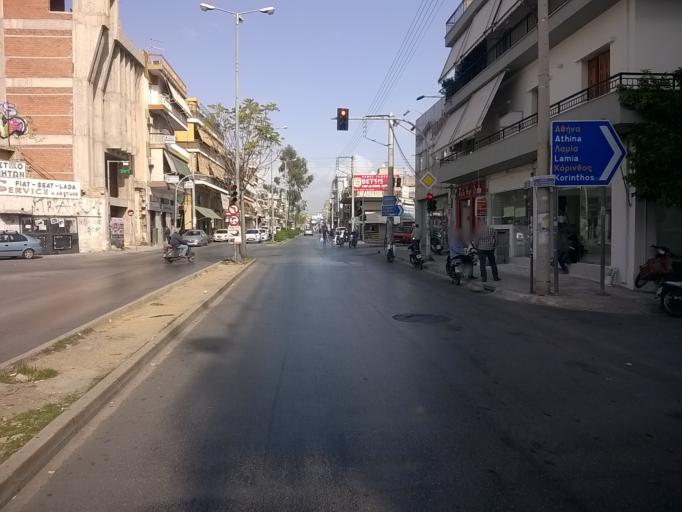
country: GR
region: Attica
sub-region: Nomos Piraios
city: Agios Ioannis Rentis
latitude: 37.9632
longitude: 23.6582
